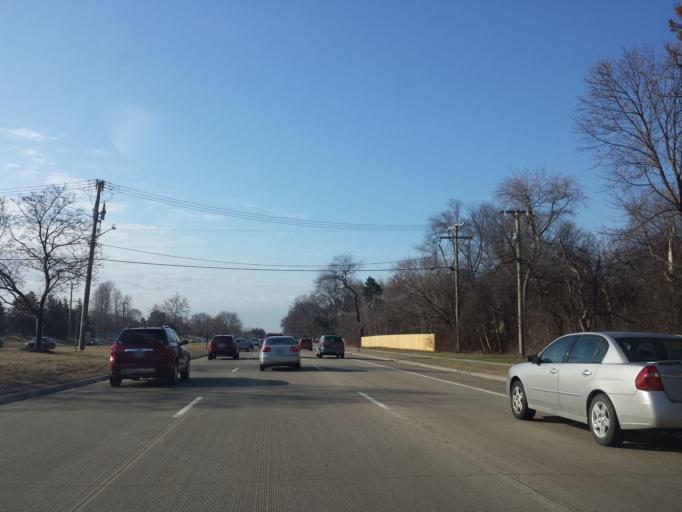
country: US
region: Michigan
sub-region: Oakland County
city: Franklin
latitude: 42.5547
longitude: -83.2855
